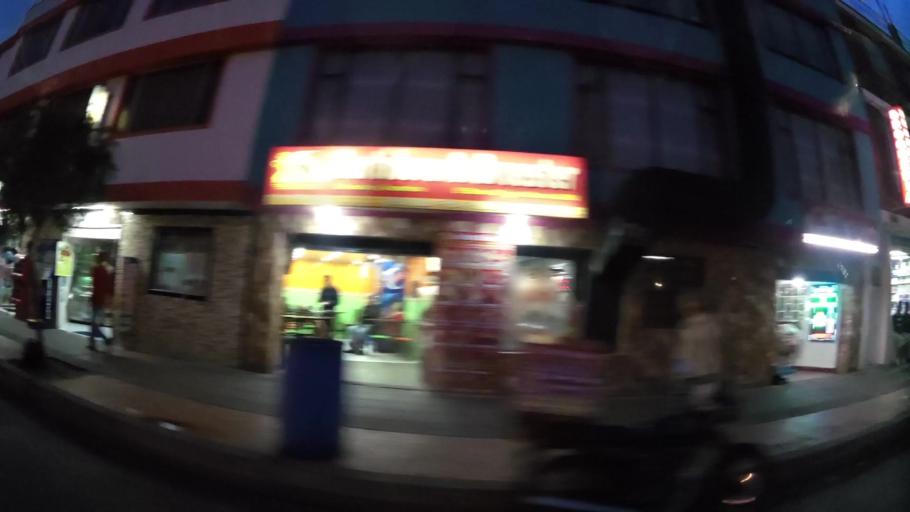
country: CO
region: Bogota D.C.
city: Bogota
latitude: 4.5791
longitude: -74.1343
